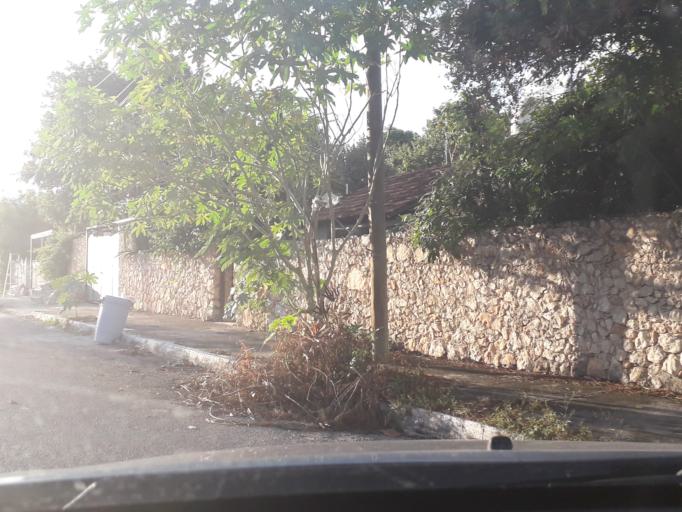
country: MX
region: Yucatan
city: Merida
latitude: 20.9756
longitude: -89.6472
